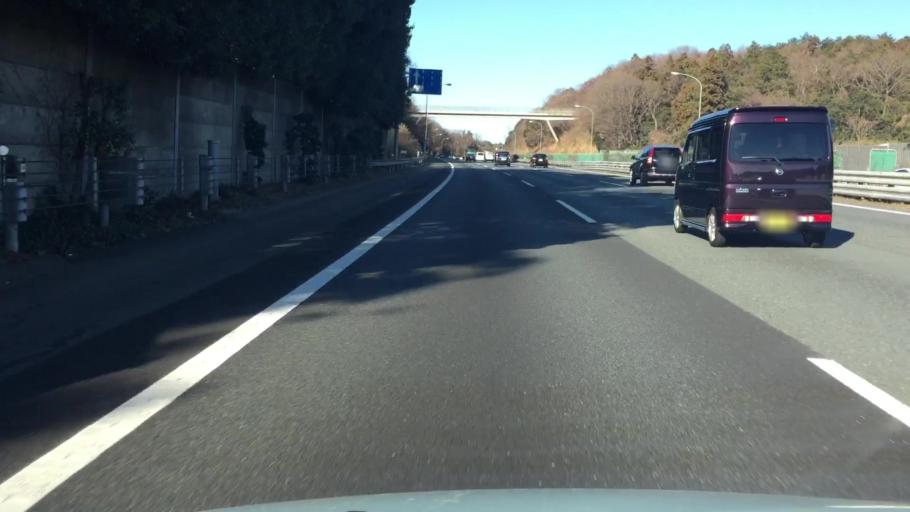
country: JP
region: Saitama
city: Ogawa
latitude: 36.0544
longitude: 139.3380
